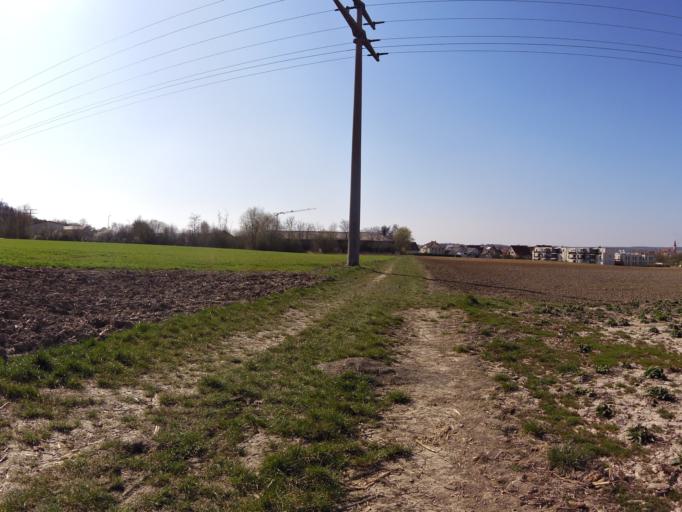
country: DE
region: Bavaria
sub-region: Regierungsbezirk Unterfranken
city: Kurnach
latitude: 49.8409
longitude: 10.0515
